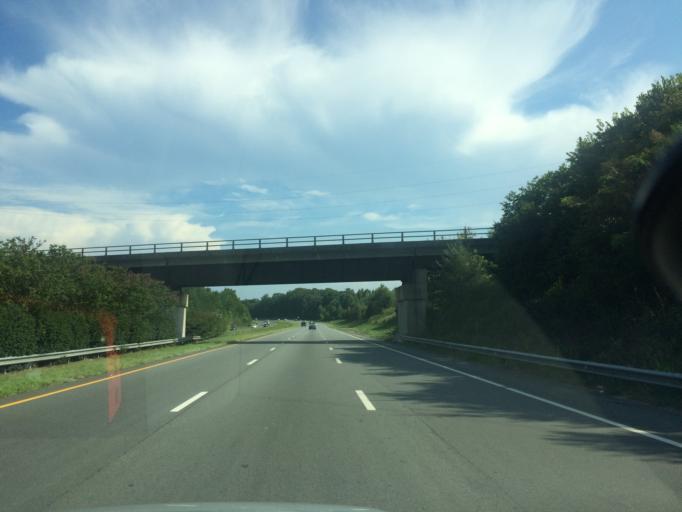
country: US
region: North Carolina
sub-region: Lincoln County
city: Lincolnton
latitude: 35.4776
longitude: -81.2296
